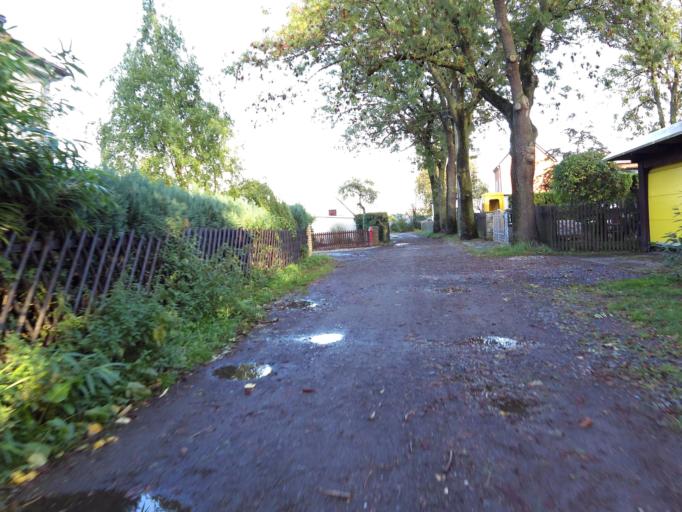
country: DE
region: Saxony
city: Taucha
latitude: 51.3224
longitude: 12.4700
